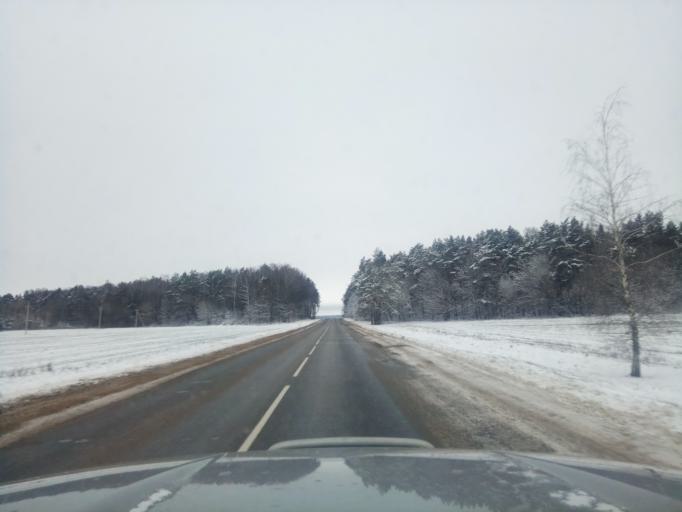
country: BY
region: Minsk
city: Kapyl'
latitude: 53.1559
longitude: 27.1112
